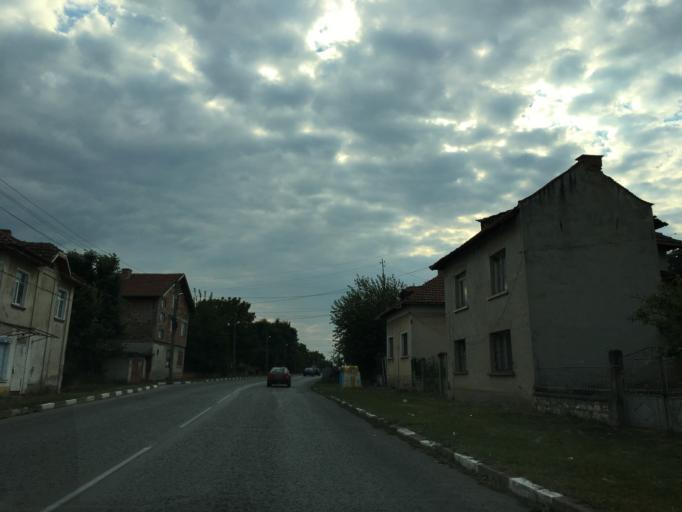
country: BG
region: Vratsa
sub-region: Obshtina Borovan
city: Borovan
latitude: 43.4226
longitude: 23.7500
